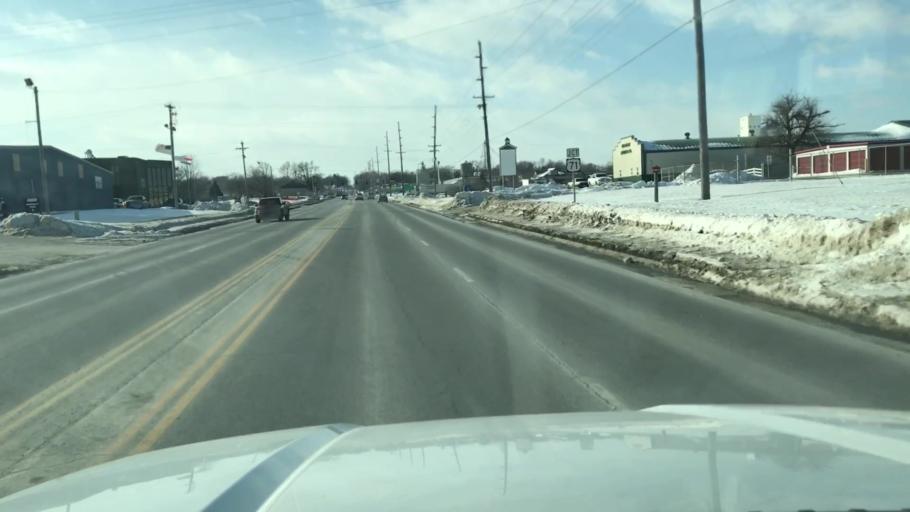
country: US
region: Missouri
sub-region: Nodaway County
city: Maryville
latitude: 40.3452
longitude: -94.8485
